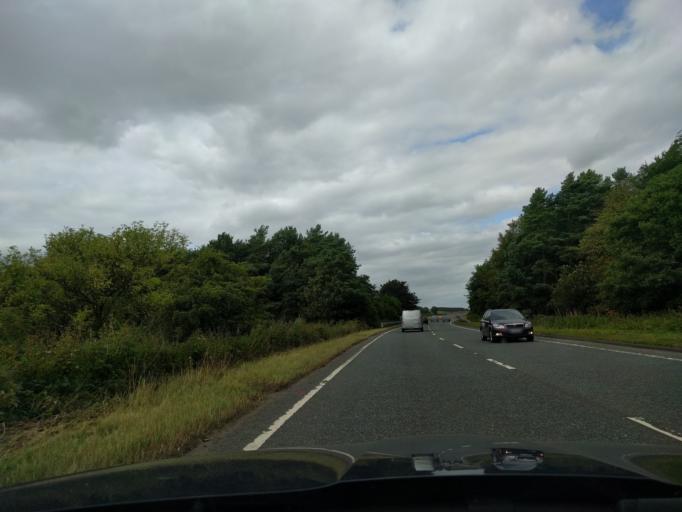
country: GB
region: England
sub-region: Northumberland
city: Ellingham
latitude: 55.4904
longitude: -1.7311
